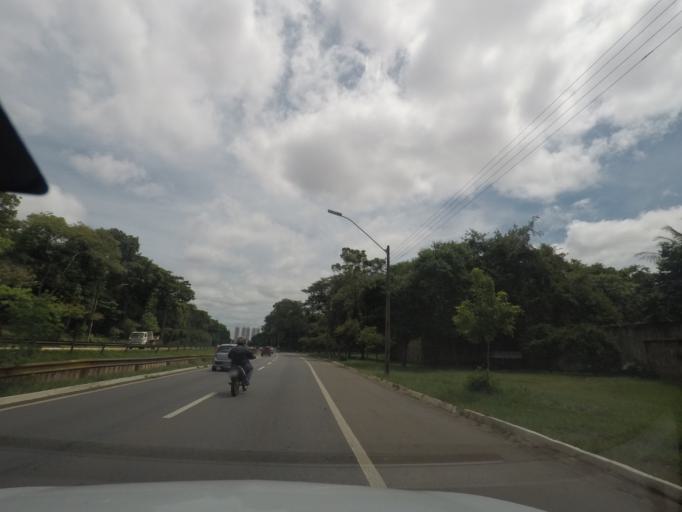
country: BR
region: Goias
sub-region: Goiania
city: Goiania
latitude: -16.6693
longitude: -49.2506
